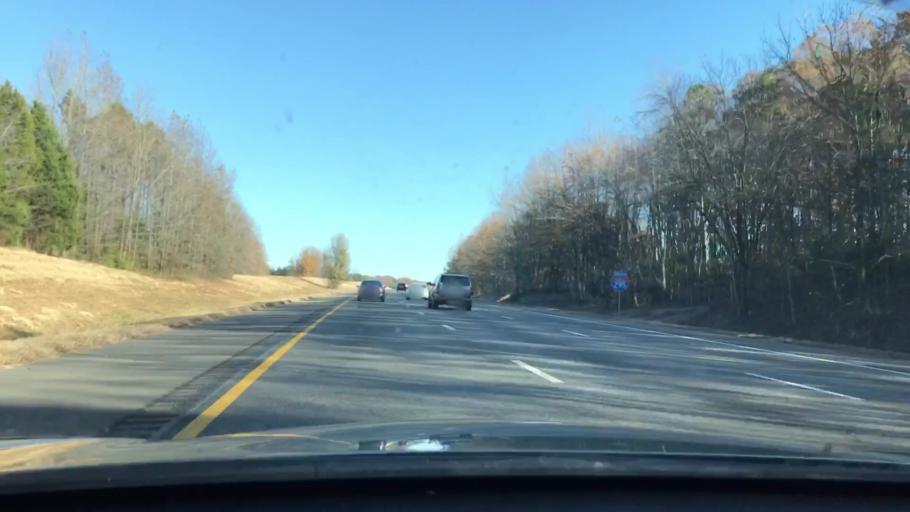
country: US
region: Virginia
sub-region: Henrico County
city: Glen Allen
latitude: 37.6818
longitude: -77.5304
